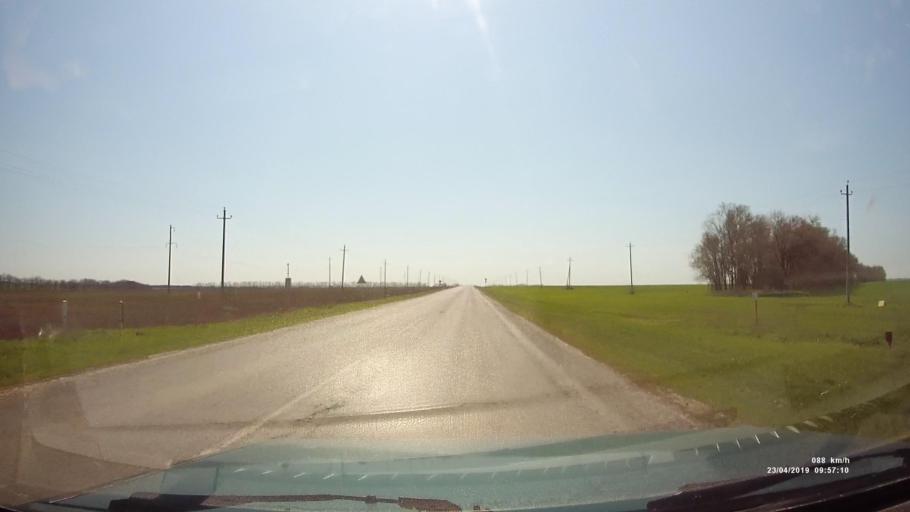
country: RU
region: Rostov
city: Orlovskiy
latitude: 46.7914
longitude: 42.0818
